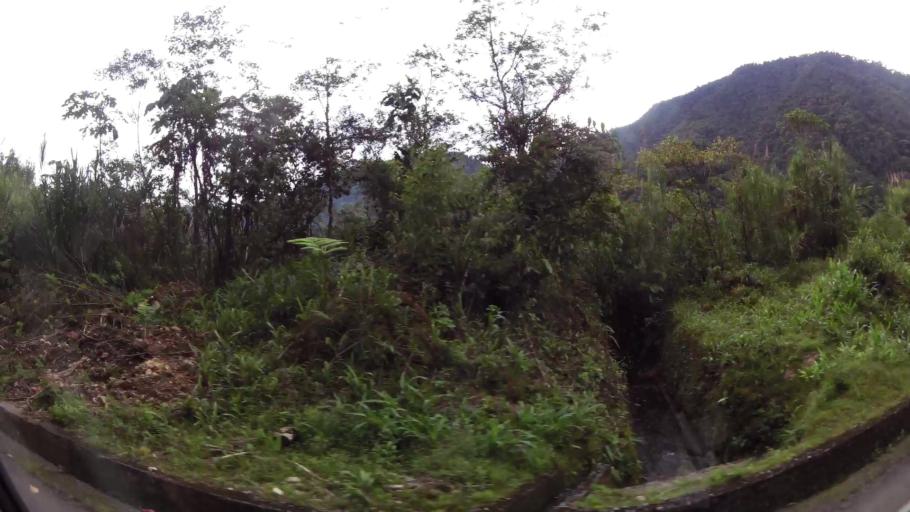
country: EC
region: Pastaza
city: Puyo
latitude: -1.4314
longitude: -78.1764
